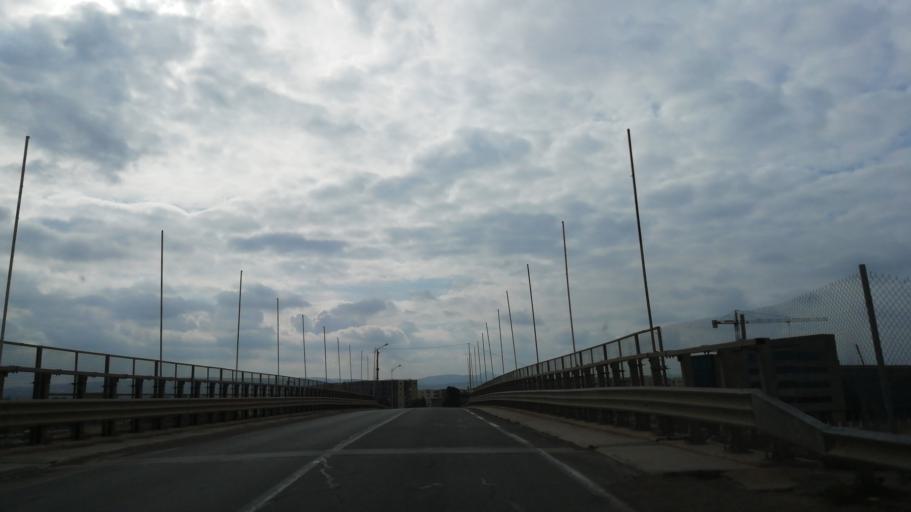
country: DZ
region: Oran
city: Sidi ech Chahmi
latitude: 35.5610
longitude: -0.4473
